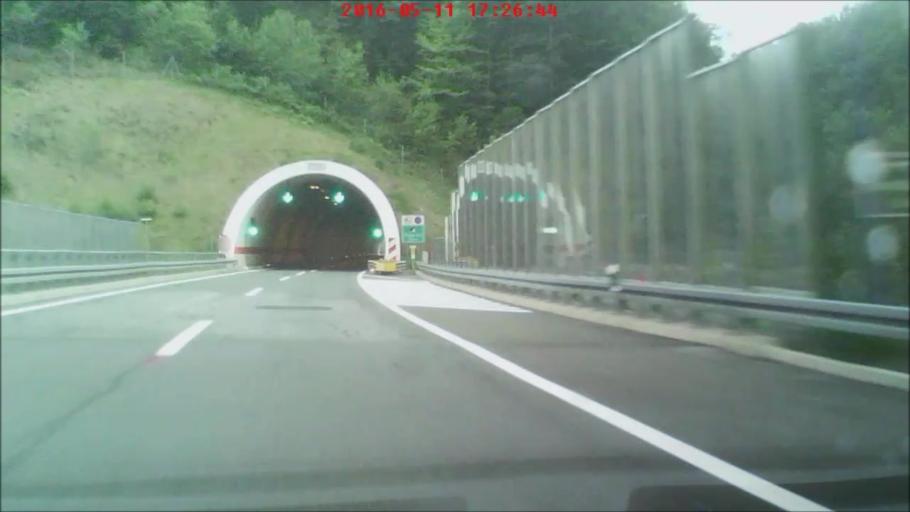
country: SI
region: Zetale
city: Zetale
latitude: 46.2518
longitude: 15.8525
